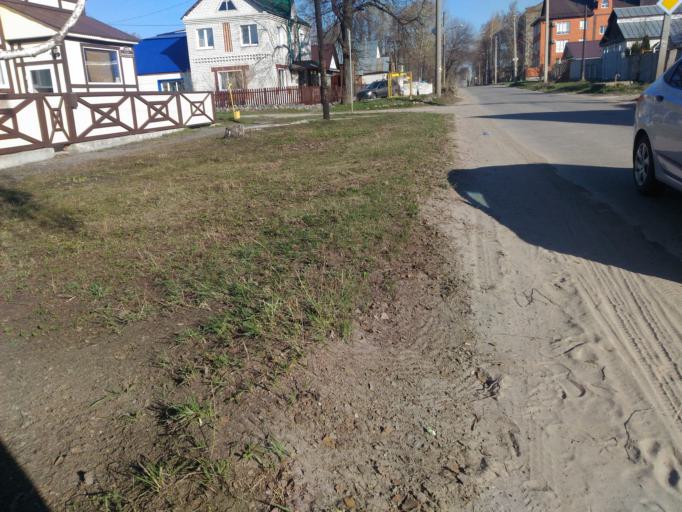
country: RU
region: Ulyanovsk
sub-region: Ulyanovskiy Rayon
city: Ulyanovsk
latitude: 54.3446
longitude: 48.3828
